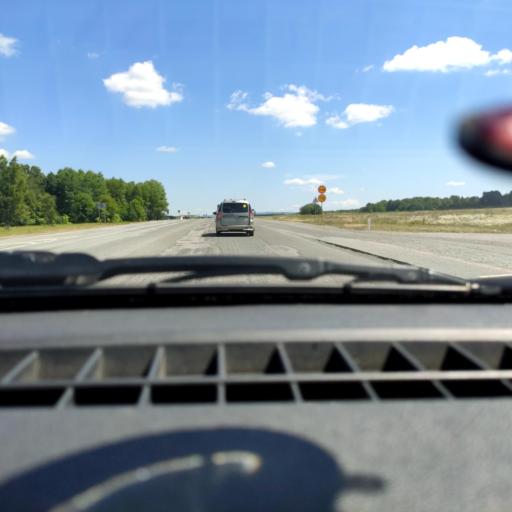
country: RU
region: Bashkortostan
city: Kudeyevskiy
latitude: 54.8172
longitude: 56.7936
